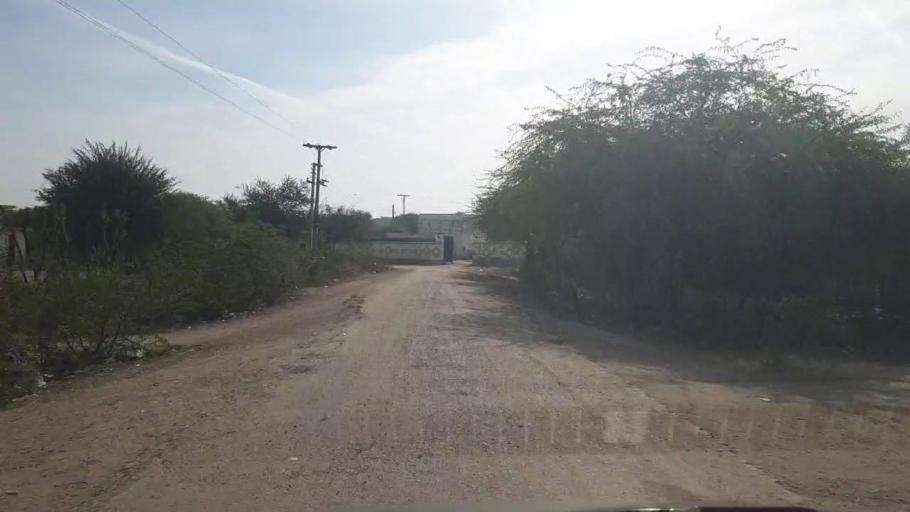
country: PK
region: Sindh
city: Umarkot
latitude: 25.3109
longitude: 69.7042
